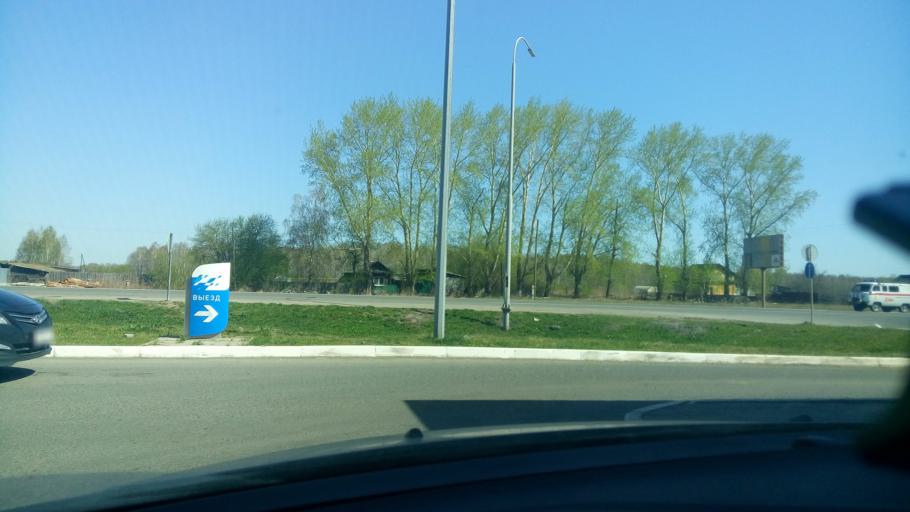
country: RU
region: Sverdlovsk
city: Bogdanovich
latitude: 56.7527
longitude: 62.0943
